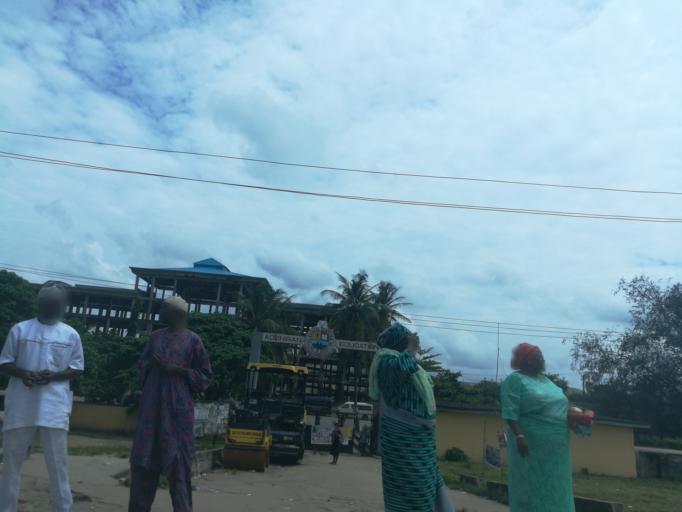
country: NG
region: Lagos
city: Ikotun
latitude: 6.4981
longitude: 3.1120
